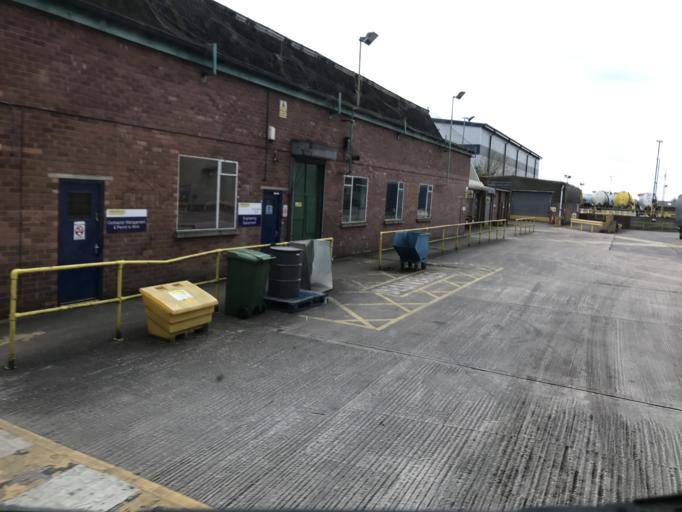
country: GB
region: England
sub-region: Trafford
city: Trafford Park
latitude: 53.4686
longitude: -2.3006
